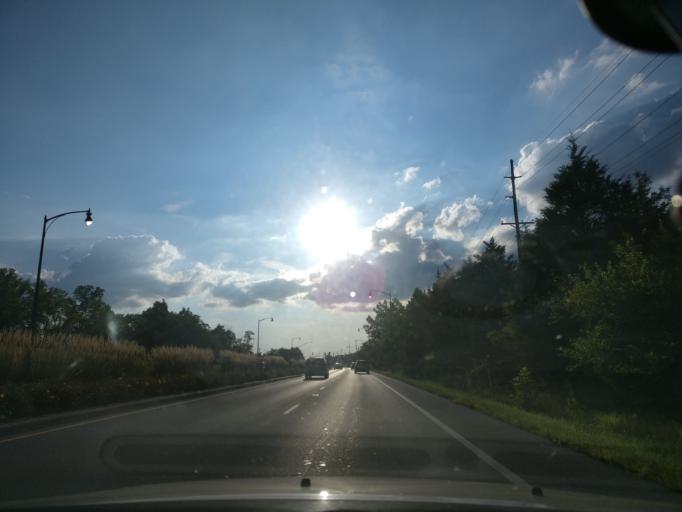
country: US
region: Ohio
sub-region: Warren County
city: Springboro
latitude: 39.5613
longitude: -84.2501
